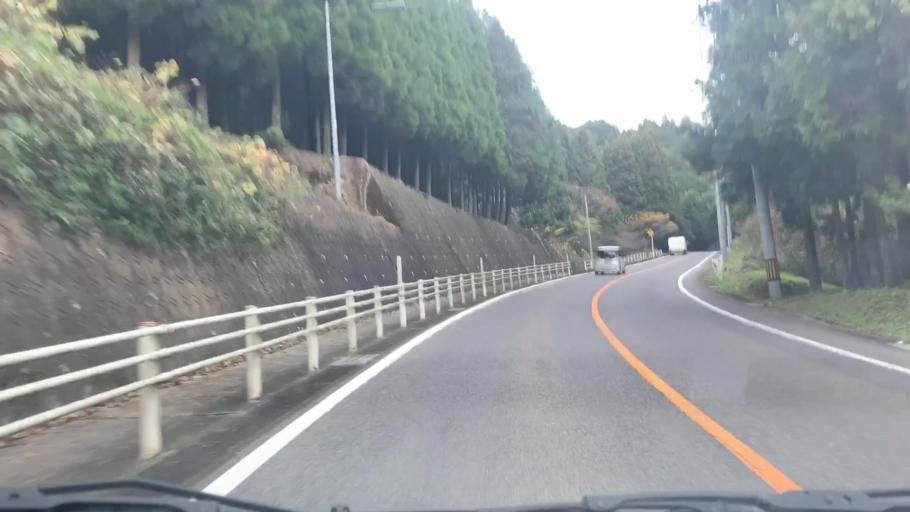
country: JP
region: Saga Prefecture
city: Ureshinomachi-shimojuku
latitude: 33.1604
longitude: 129.9682
